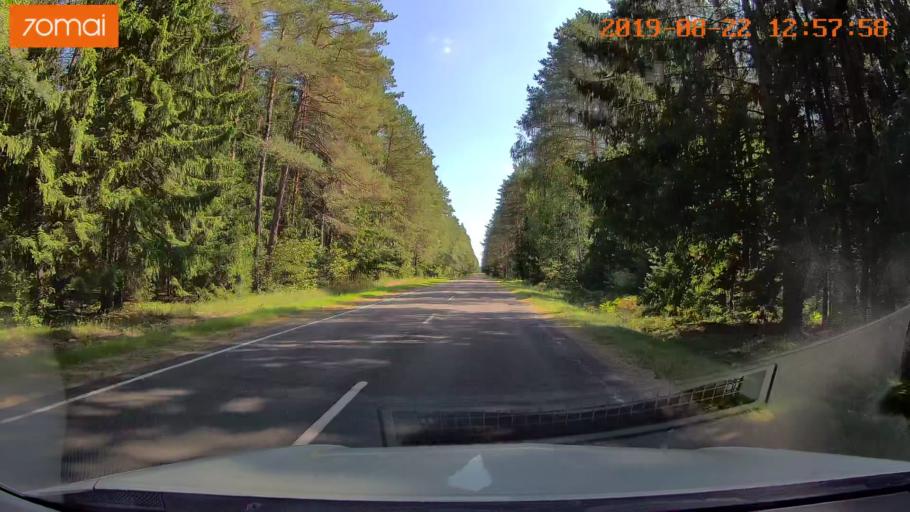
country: BY
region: Minsk
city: Prawdzinski
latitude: 53.4265
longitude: 27.7600
